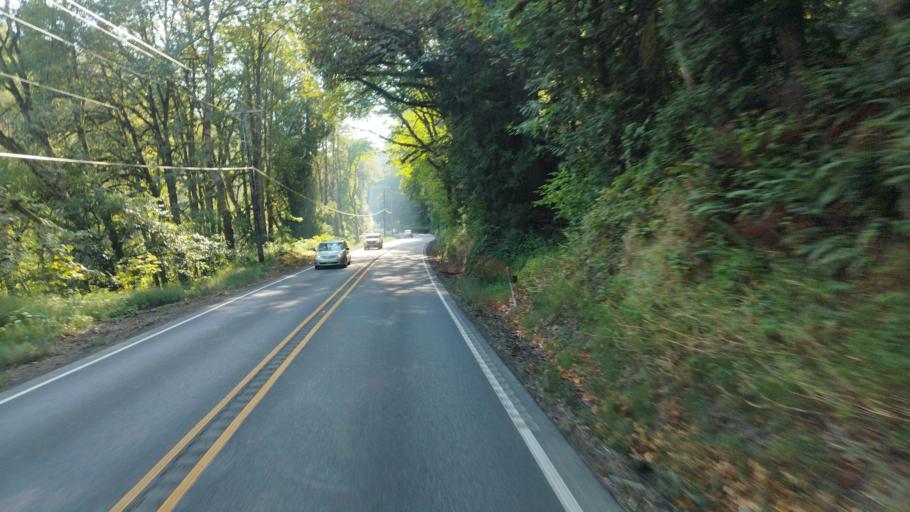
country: US
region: Oregon
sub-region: Washington County
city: Bethany
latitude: 45.6490
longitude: -122.8544
